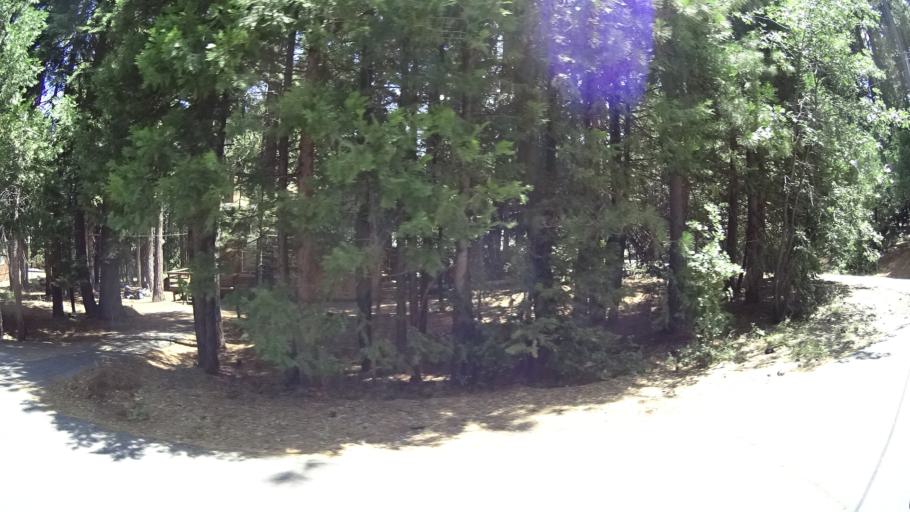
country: US
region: California
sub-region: Calaveras County
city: Arnold
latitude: 38.3031
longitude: -120.2583
